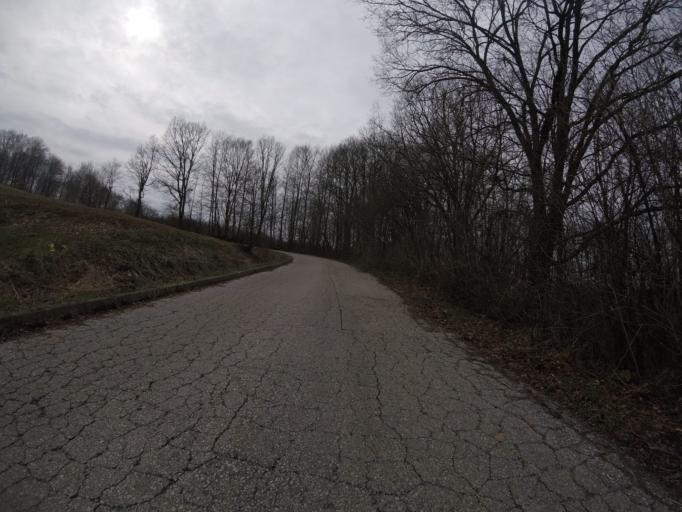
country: HR
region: Grad Zagreb
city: Strmec
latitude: 45.5857
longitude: 15.9500
